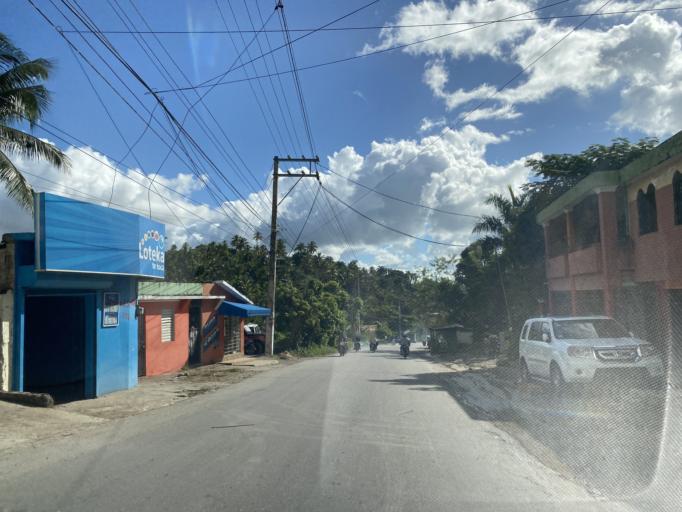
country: DO
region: Samana
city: Samana
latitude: 19.2071
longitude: -69.3501
